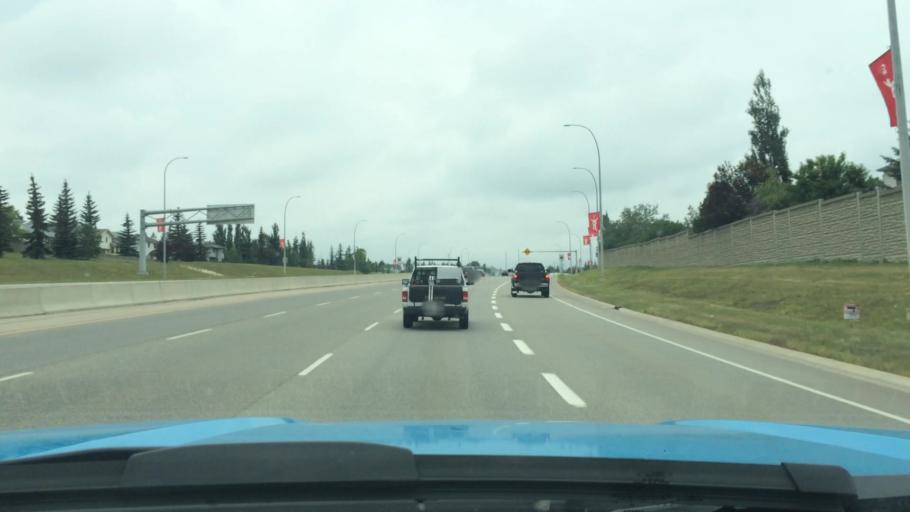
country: CA
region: Alberta
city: Calgary
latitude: 51.1426
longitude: -114.1022
